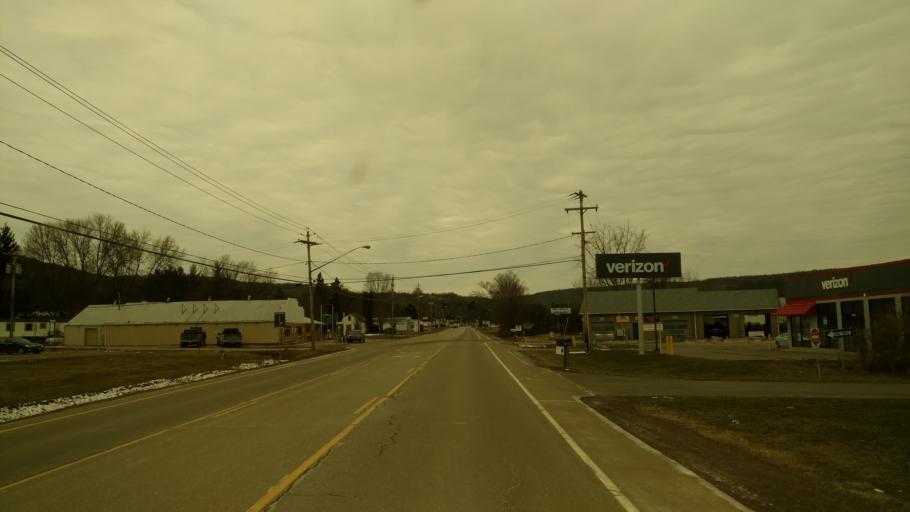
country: US
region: New York
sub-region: Allegany County
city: Wellsville
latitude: 42.1261
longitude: -77.9692
